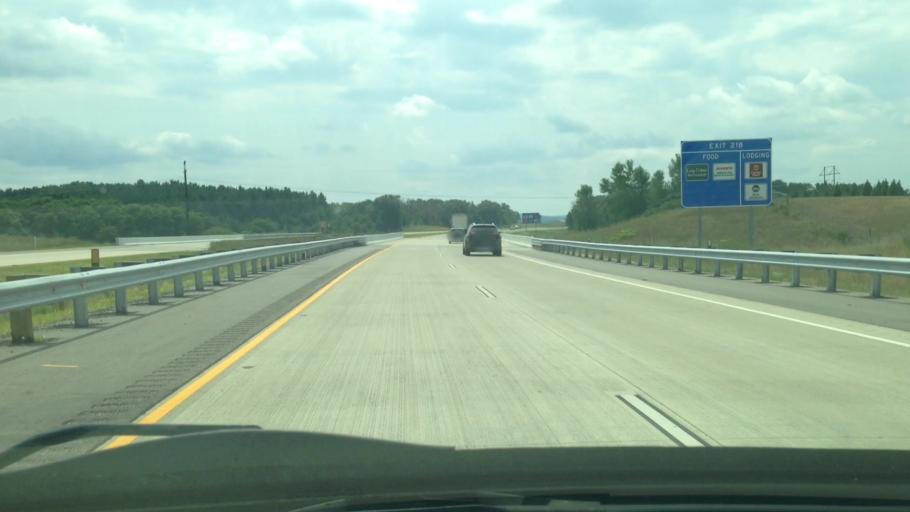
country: US
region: Wisconsin
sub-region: Sauk County
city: West Baraboo
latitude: 43.4864
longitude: -89.7772
